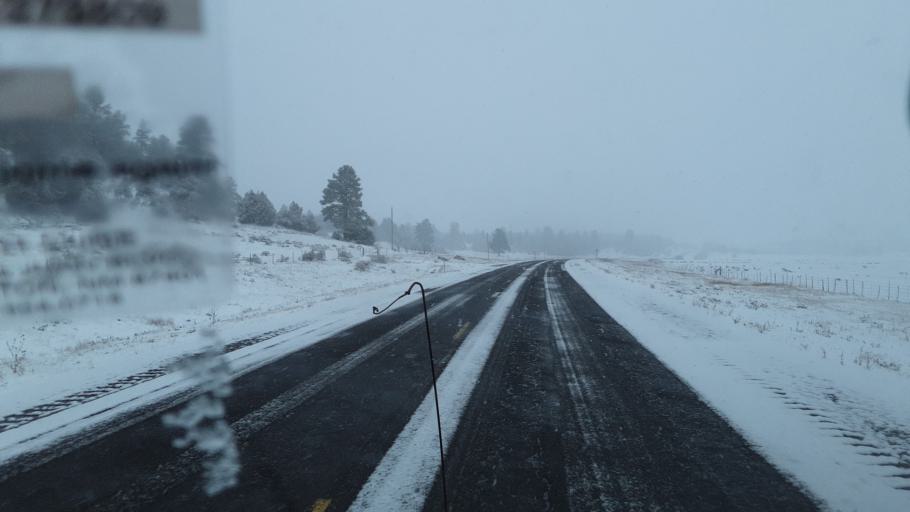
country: US
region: New Mexico
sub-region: Rio Arriba County
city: Dulce
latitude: 36.9153
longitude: -106.7969
